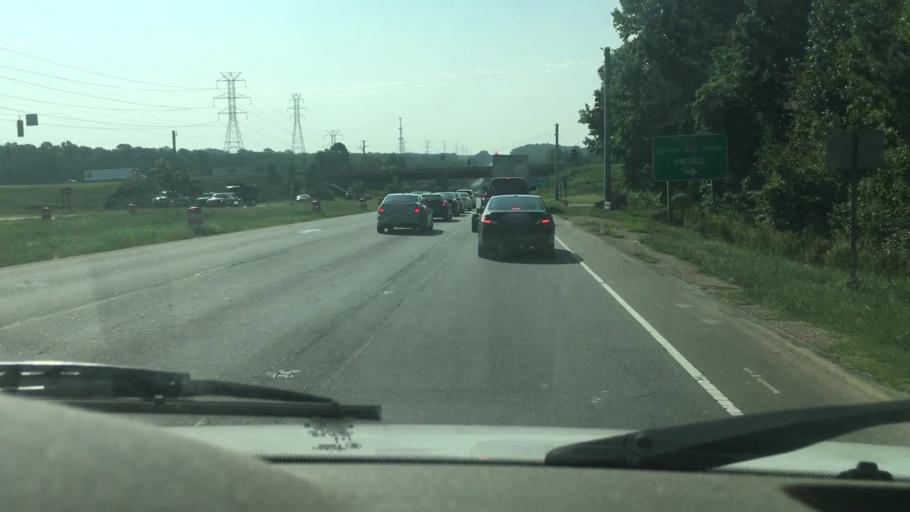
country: US
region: North Carolina
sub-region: Gaston County
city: Mount Holly
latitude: 35.3234
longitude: -80.9428
